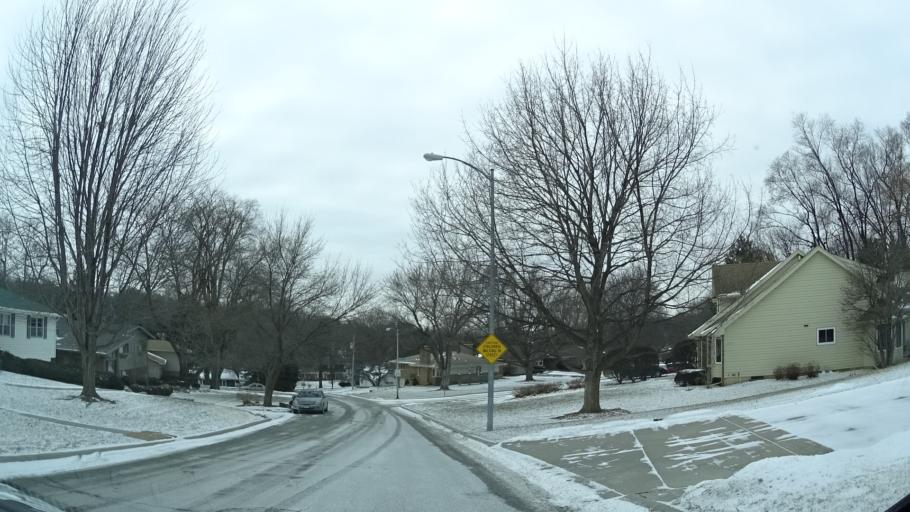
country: US
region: Nebraska
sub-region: Douglas County
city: Omaha
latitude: 41.2703
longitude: -96.0049
